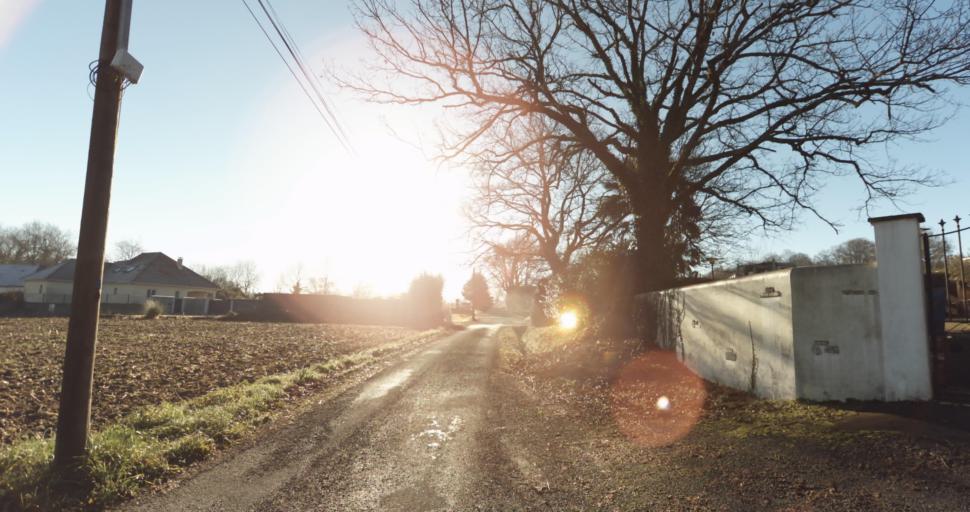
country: FR
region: Aquitaine
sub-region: Departement des Pyrenees-Atlantiques
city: Morlaas
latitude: 43.3391
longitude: -0.2628
